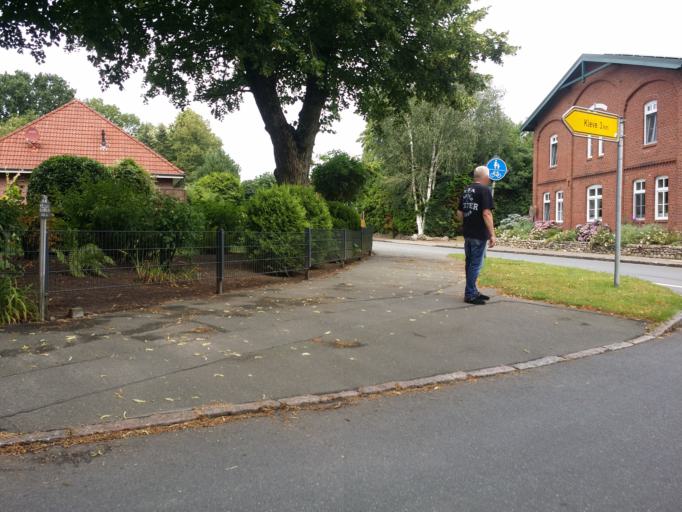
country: DE
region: Schleswig-Holstein
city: Huje
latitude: 53.9771
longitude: 9.4344
